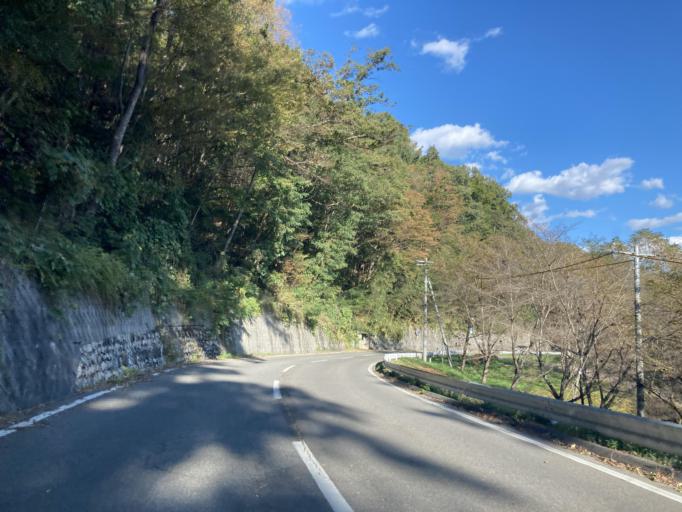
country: JP
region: Nagano
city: Omachi
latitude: 36.4409
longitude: 137.9906
